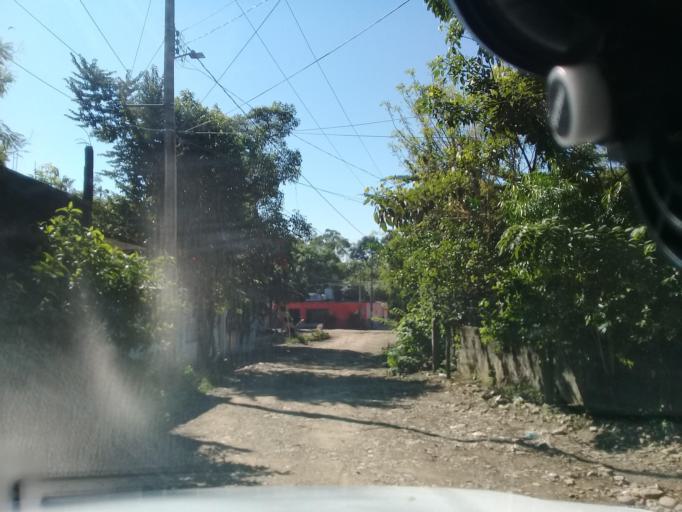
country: MX
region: Hidalgo
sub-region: Huejutla de Reyes
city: Huejutla de Reyes
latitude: 21.1617
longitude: -98.4130
